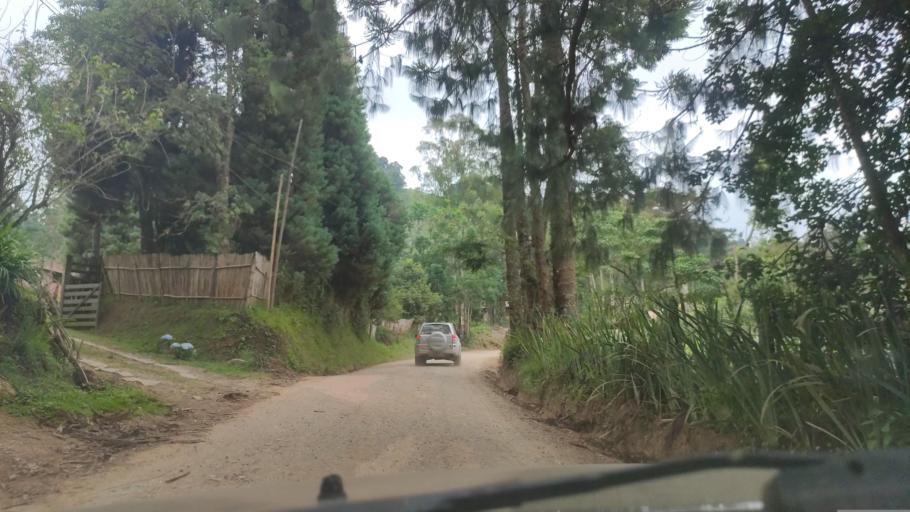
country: BR
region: Minas Gerais
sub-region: Paraisopolis
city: Paraisopolis
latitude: -22.6637
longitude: -45.8699
